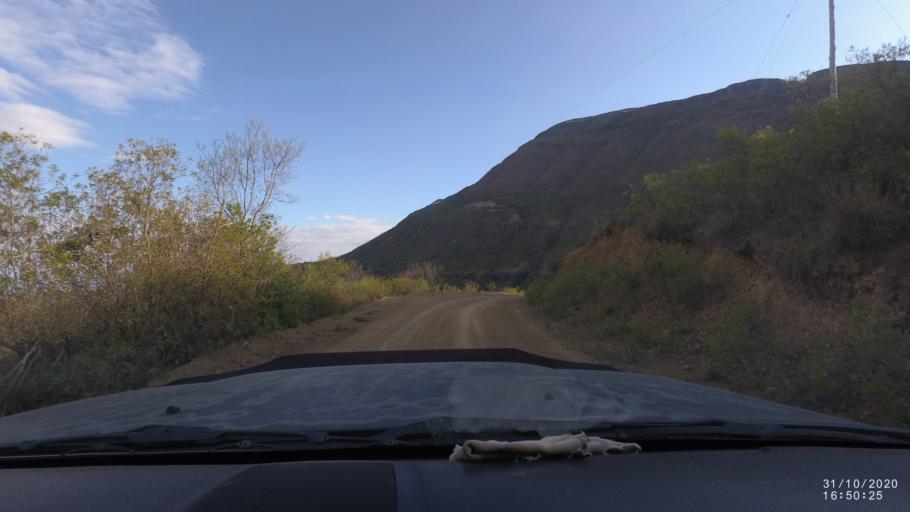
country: BO
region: Chuquisaca
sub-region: Provincia Zudanez
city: Mojocoya
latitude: -18.5087
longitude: -64.5705
